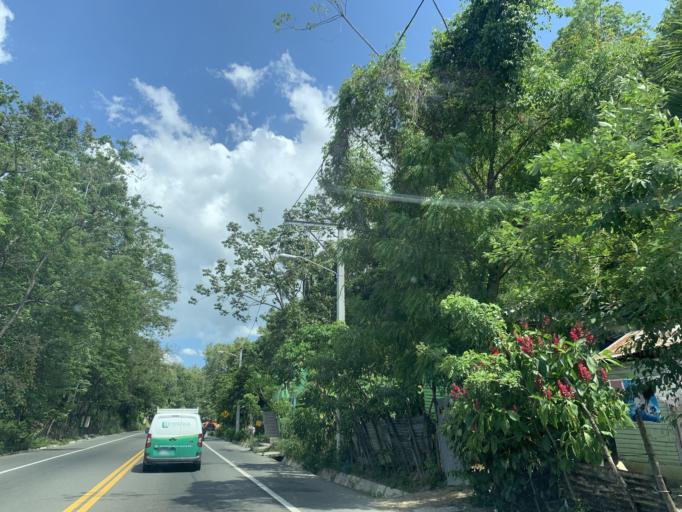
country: DO
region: Puerto Plata
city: Altamira
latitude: 19.6678
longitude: -70.8311
